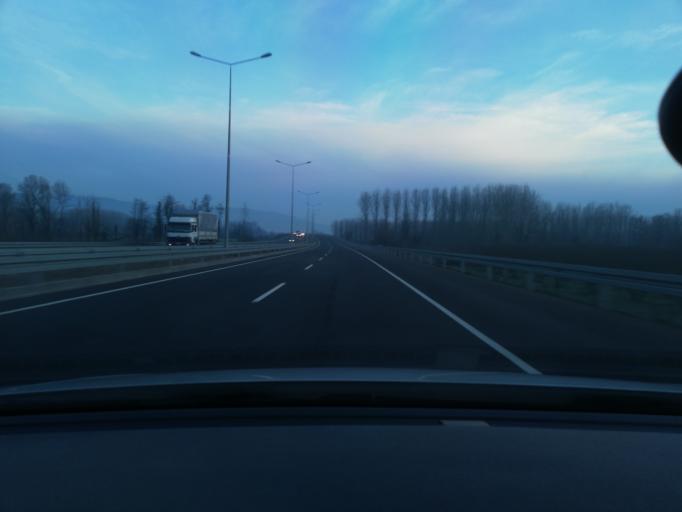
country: TR
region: Duzce
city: Duzce
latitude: 40.8125
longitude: 31.1692
